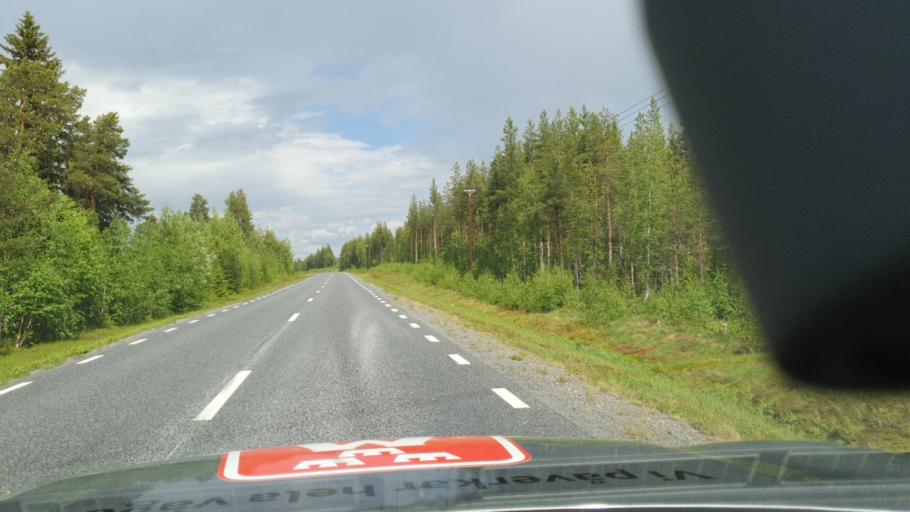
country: SE
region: Vaesterbotten
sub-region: Asele Kommun
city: Asele
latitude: 63.9259
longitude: 17.2592
